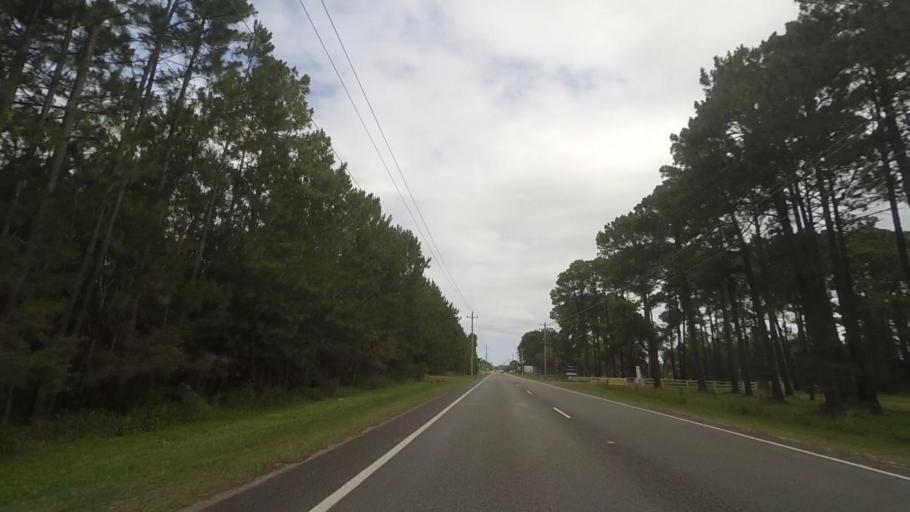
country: AU
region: New South Wales
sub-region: Great Lakes
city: Hawks Nest
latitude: -32.6483
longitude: 152.1479
